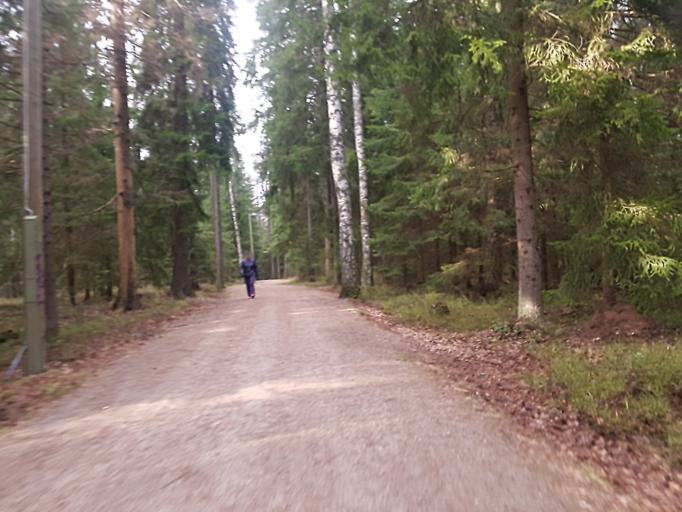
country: FI
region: Uusimaa
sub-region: Helsinki
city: Helsinki
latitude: 60.2595
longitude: 24.9302
